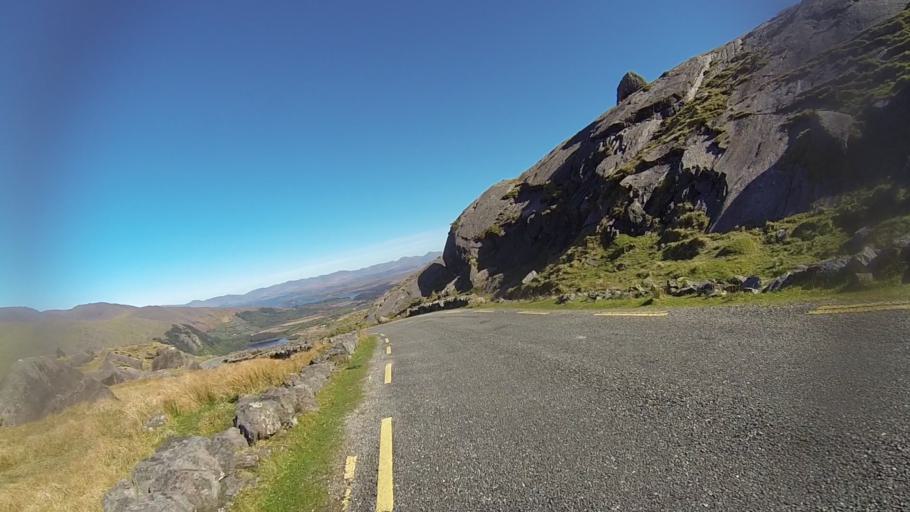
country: IE
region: Munster
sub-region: Ciarrai
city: Kenmare
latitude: 51.7230
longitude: -9.7573
